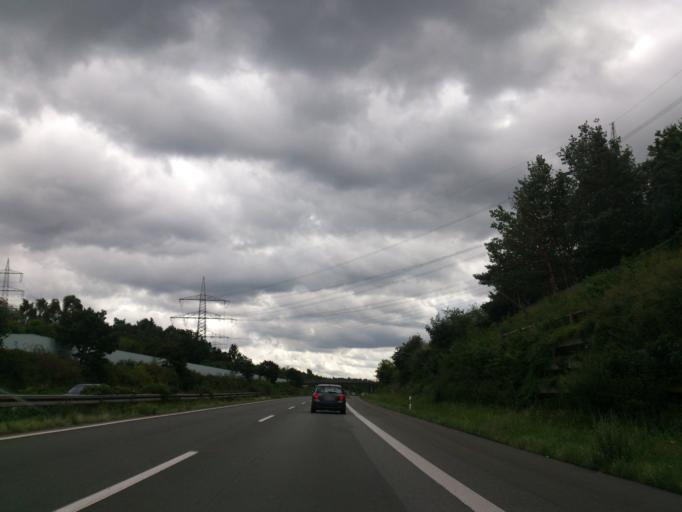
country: DE
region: North Rhine-Westphalia
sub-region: Regierungsbezirk Detmold
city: Oerlinghausen
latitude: 51.8965
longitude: 8.6372
